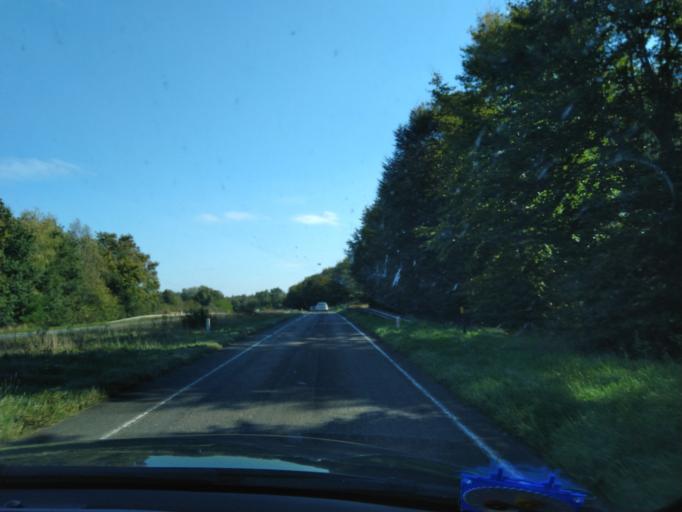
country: NL
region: Groningen
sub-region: Gemeente Veendam
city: Veendam
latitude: 53.0953
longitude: 6.9033
